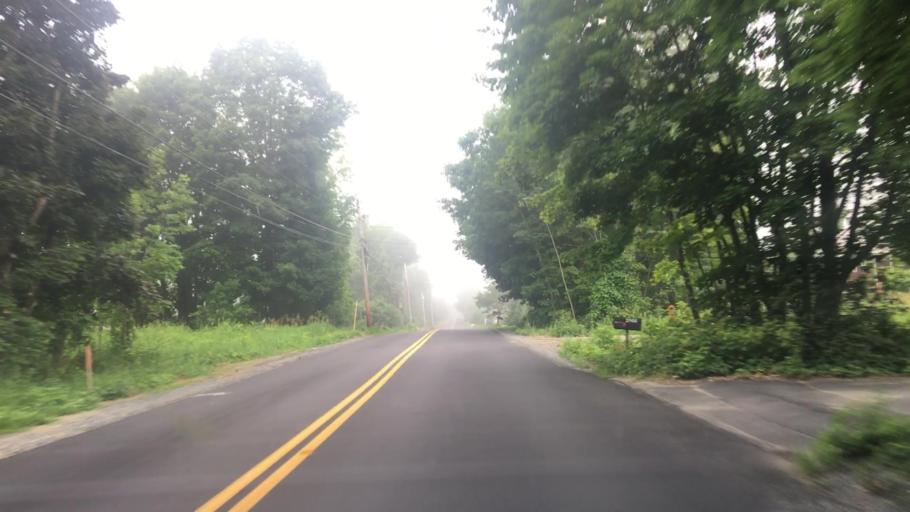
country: US
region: Maine
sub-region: Kennebec County
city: Oakland
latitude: 44.5167
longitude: -69.7185
